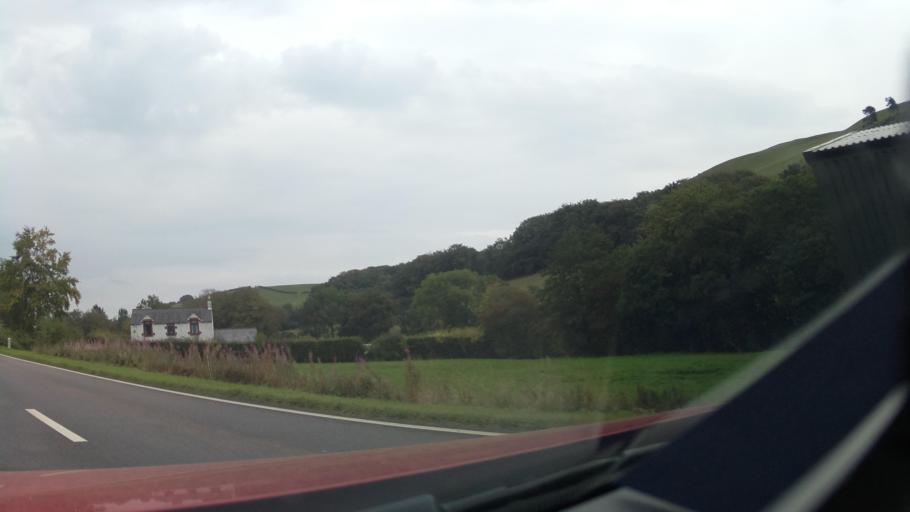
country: GB
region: Scotland
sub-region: Dumfries and Galloway
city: Locharbriggs
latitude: 55.1358
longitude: -3.5620
